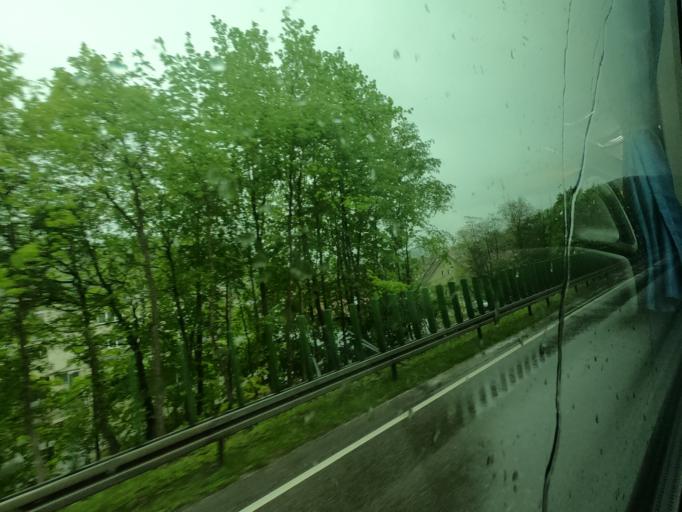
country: DE
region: Baden-Wuerttemberg
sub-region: Regierungsbezirk Stuttgart
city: Aalen
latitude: 48.8161
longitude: 10.1225
